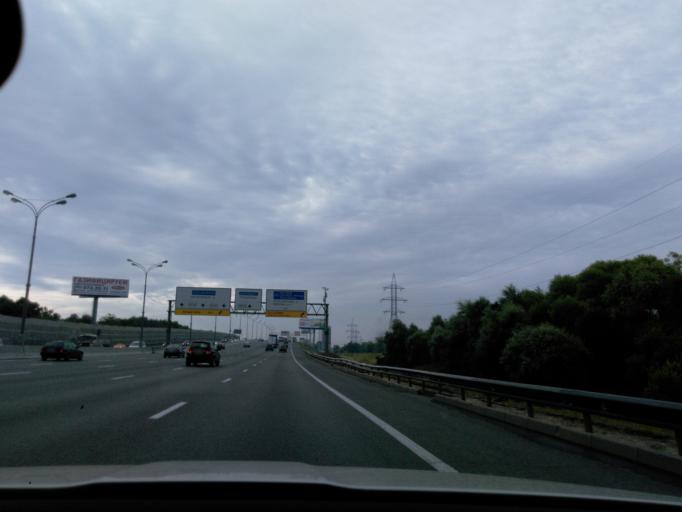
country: RU
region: Moscow
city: Yaroslavskiy
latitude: 55.8891
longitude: 37.7122
